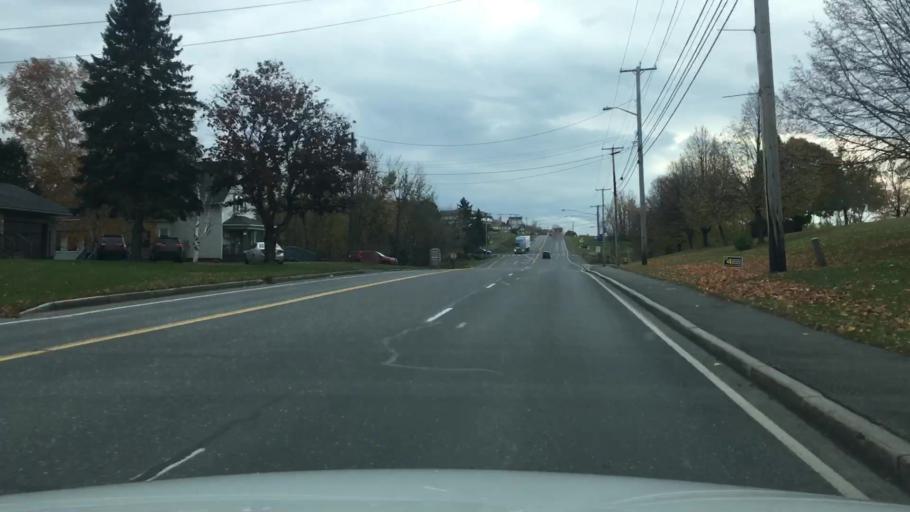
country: US
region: Maine
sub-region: Aroostook County
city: Presque Isle
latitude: 46.6718
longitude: -68.0147
